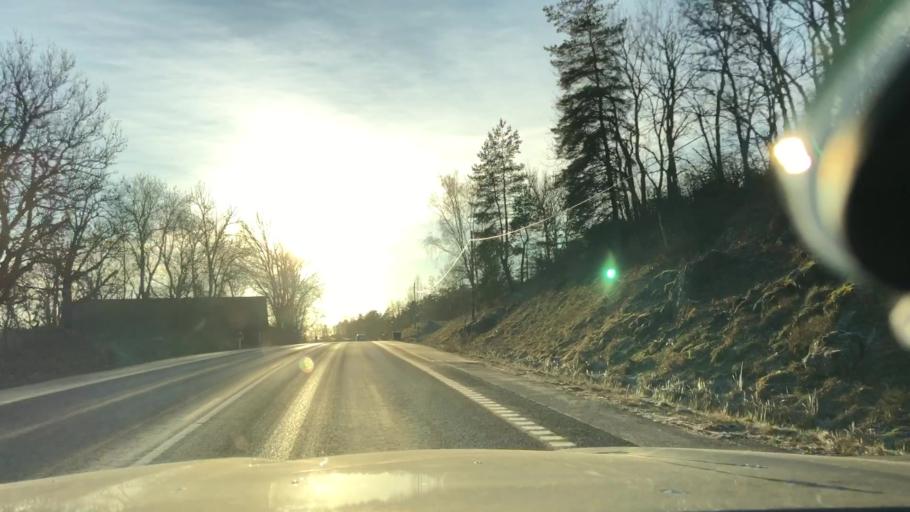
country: SE
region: Soedermanland
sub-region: Trosa Kommun
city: Vagnharad
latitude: 59.0363
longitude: 17.5998
